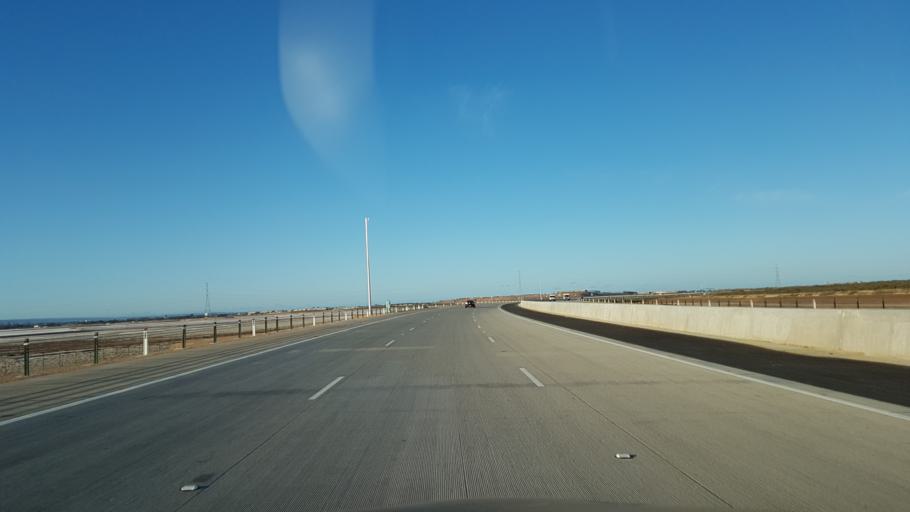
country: AU
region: South Australia
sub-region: Port Adelaide Enfield
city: Enfield
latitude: -34.8023
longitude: 138.5758
